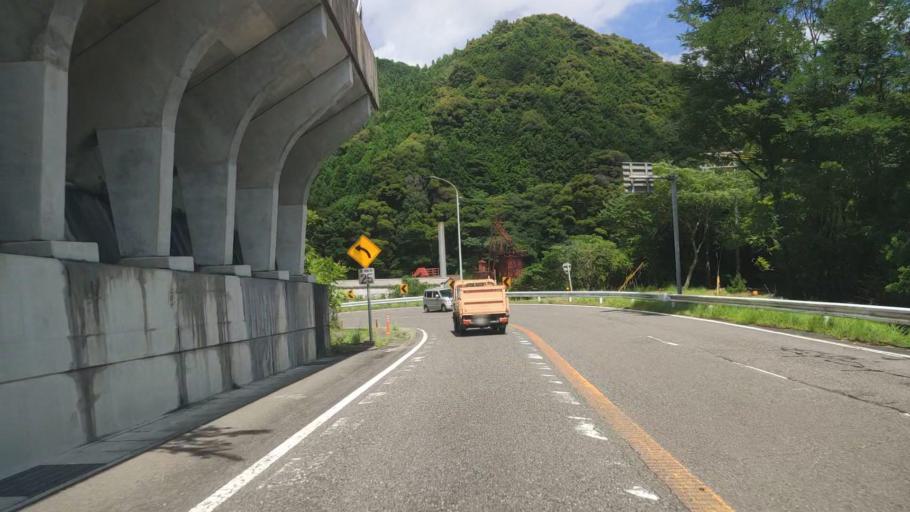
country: JP
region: Mie
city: Owase
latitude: 33.9195
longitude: 136.1061
